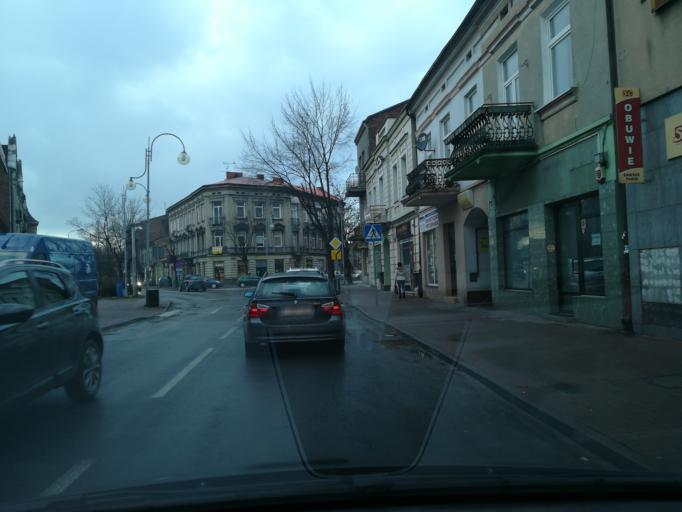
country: PL
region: Lodz Voivodeship
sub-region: Powiat radomszczanski
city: Radomsko
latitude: 51.0687
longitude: 19.4397
